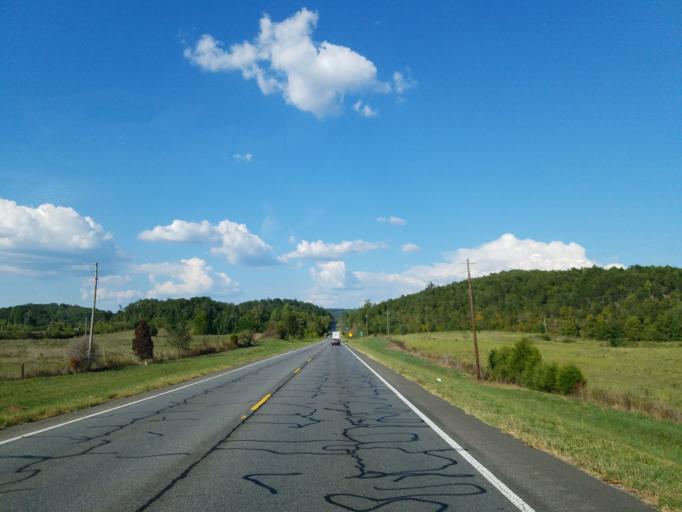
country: US
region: Georgia
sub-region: Bartow County
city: Rydal
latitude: 34.3644
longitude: -84.7151
